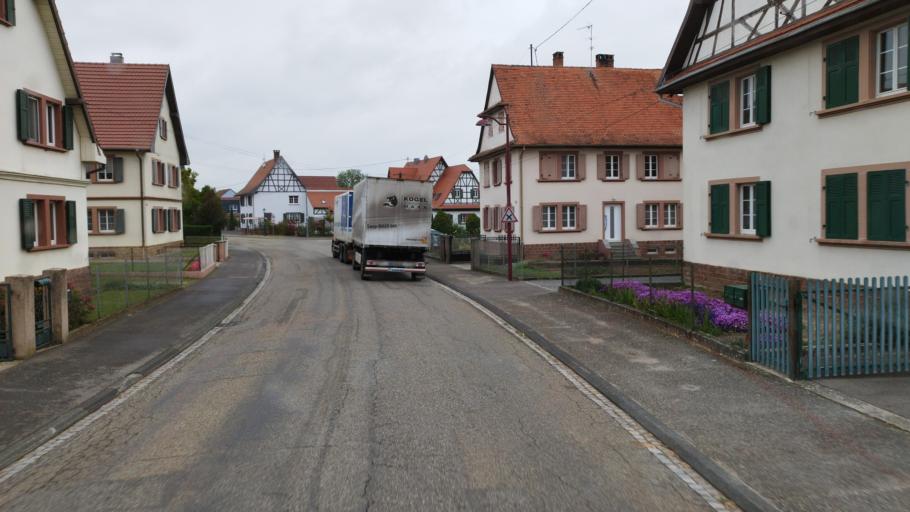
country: DE
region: Rheinland-Pfalz
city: Steinfeld
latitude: 48.9882
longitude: 8.0469
